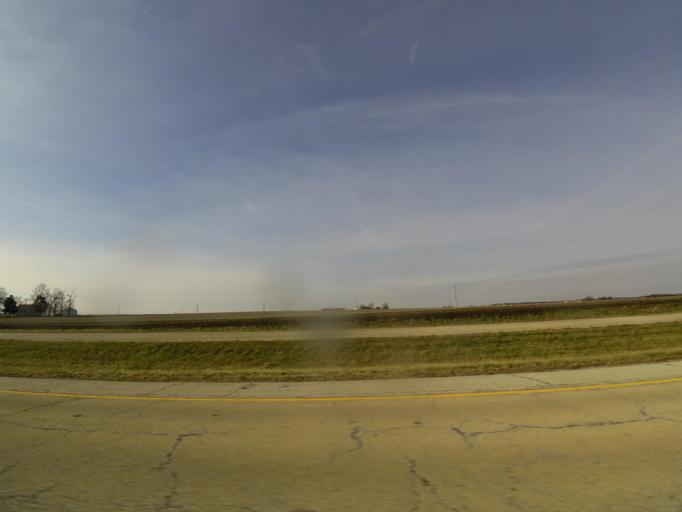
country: US
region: Illinois
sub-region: Macon County
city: Maroa
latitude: 40.0754
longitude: -88.9656
